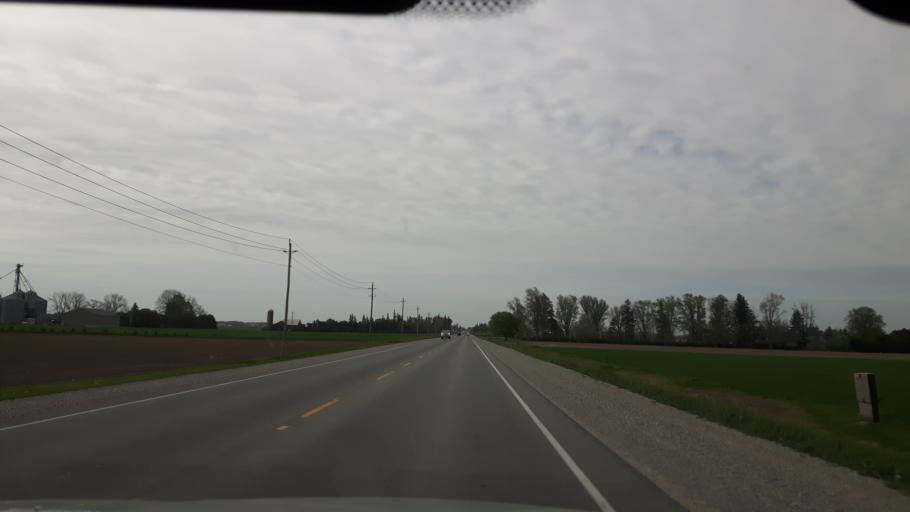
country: CA
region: Ontario
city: South Huron
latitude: 43.3852
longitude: -81.4885
